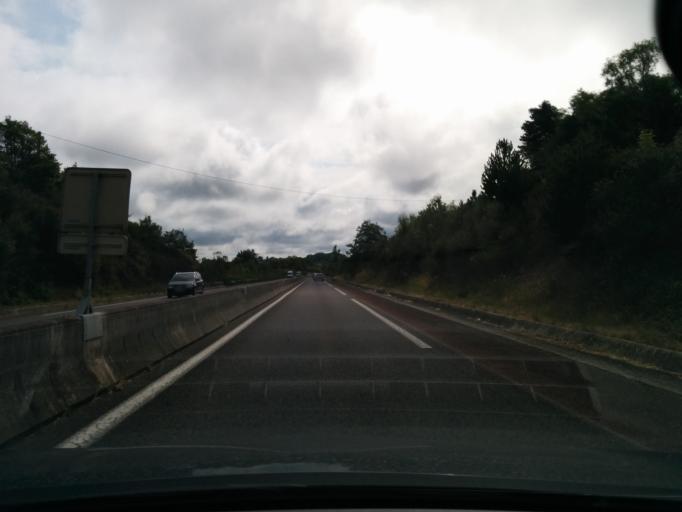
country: FR
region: Midi-Pyrenees
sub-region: Departement du Lot
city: Pradines
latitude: 44.5843
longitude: 1.4791
